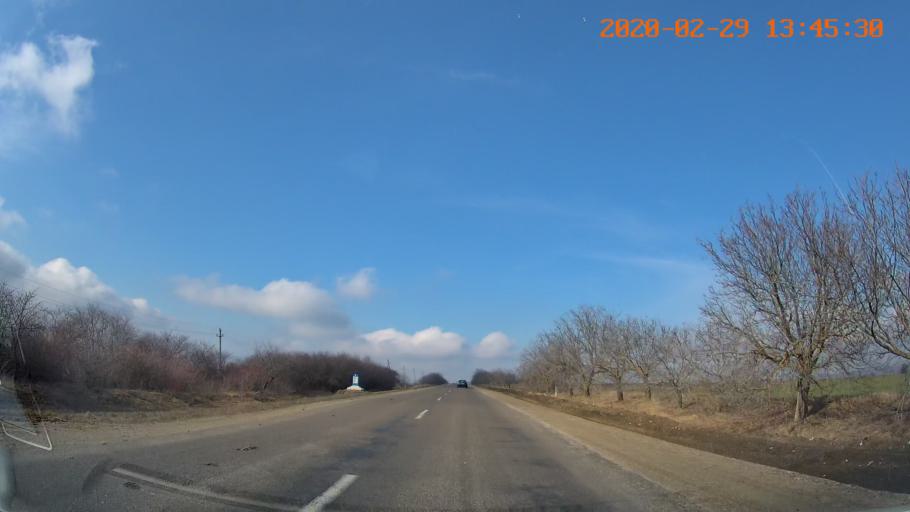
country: MD
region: Floresti
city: Leninskiy
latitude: 47.8485
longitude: 28.5146
